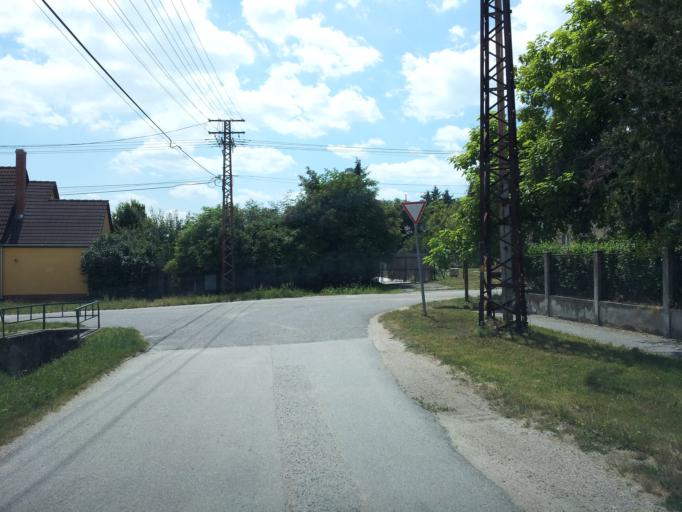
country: HU
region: Veszprem
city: Balatonkenese
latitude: 47.0361
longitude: 18.1044
